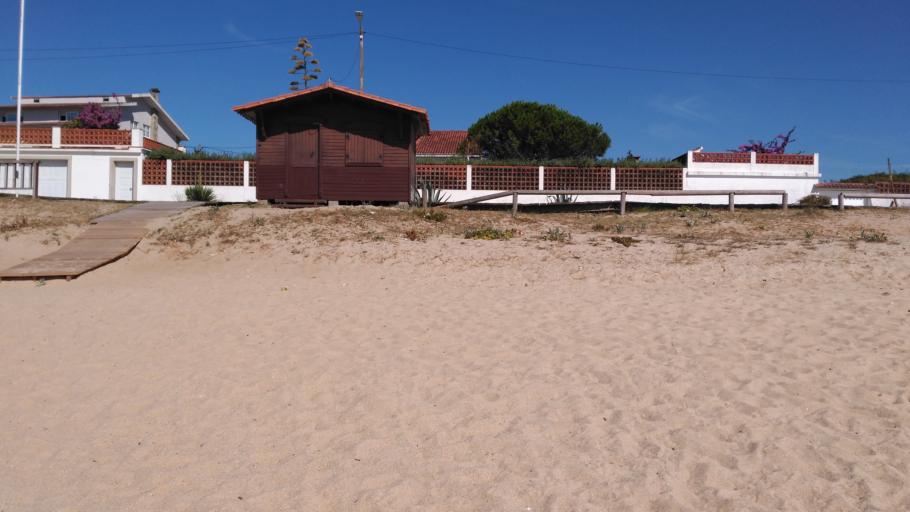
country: ES
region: Galicia
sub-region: Provincia da Coruna
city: Boiro
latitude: 42.5850
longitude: -8.9520
